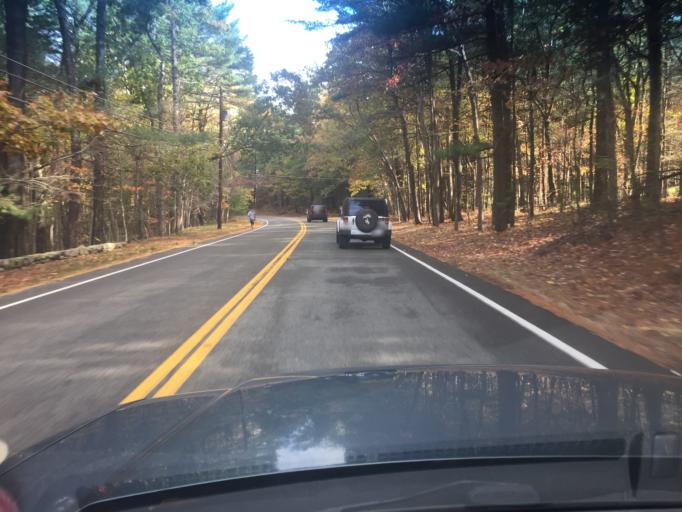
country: US
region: Massachusetts
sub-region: Norfolk County
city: Dover
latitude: 42.2232
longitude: -71.2989
